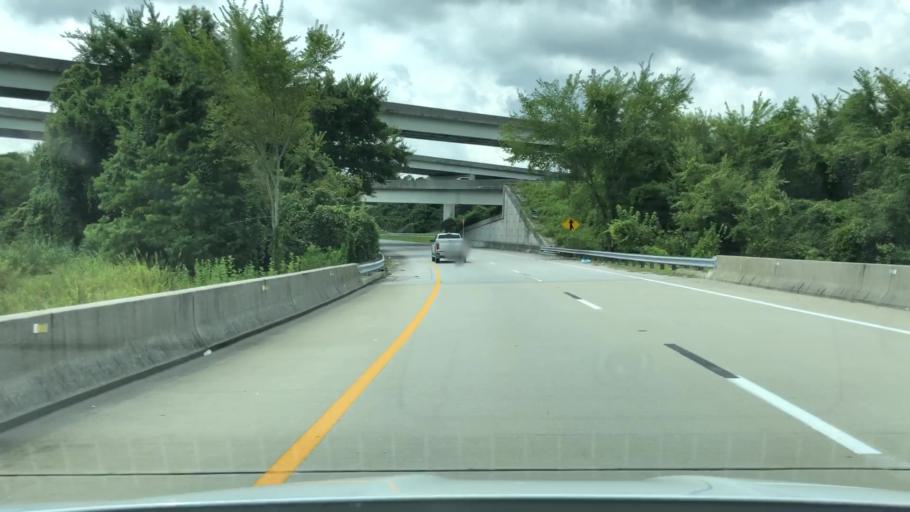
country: US
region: North Carolina
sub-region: Craven County
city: James City
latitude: 35.0955
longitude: -77.0374
